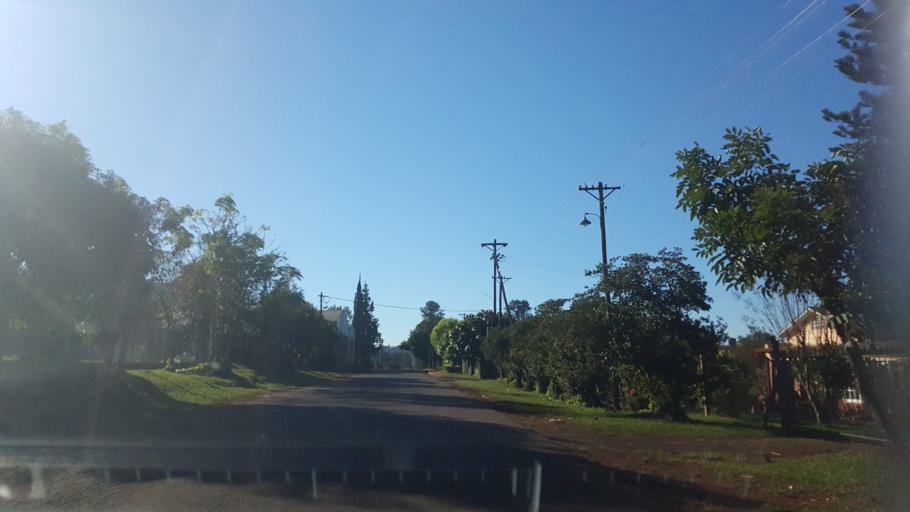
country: AR
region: Misiones
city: Jardin America
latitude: -27.0857
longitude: -55.2864
